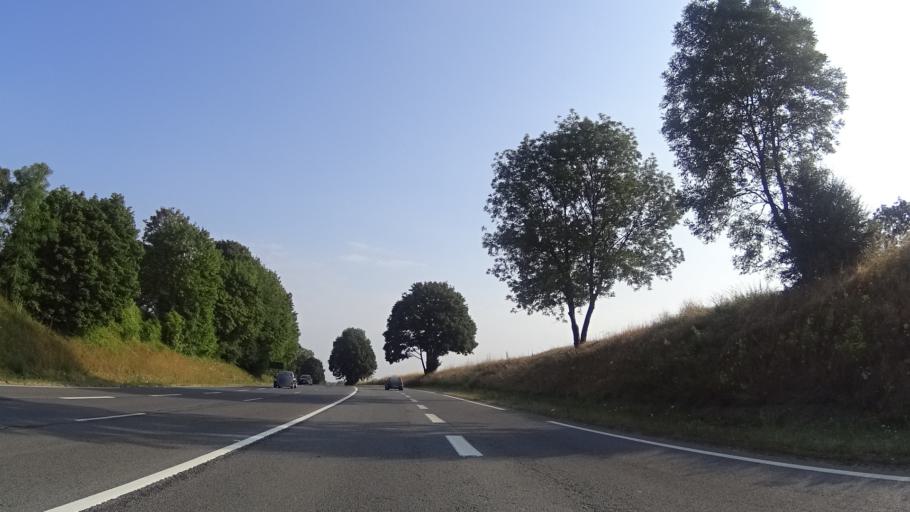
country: FR
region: Ile-de-France
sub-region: Departement du Val-d'Oise
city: Luzarches
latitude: 49.1117
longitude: 2.4303
